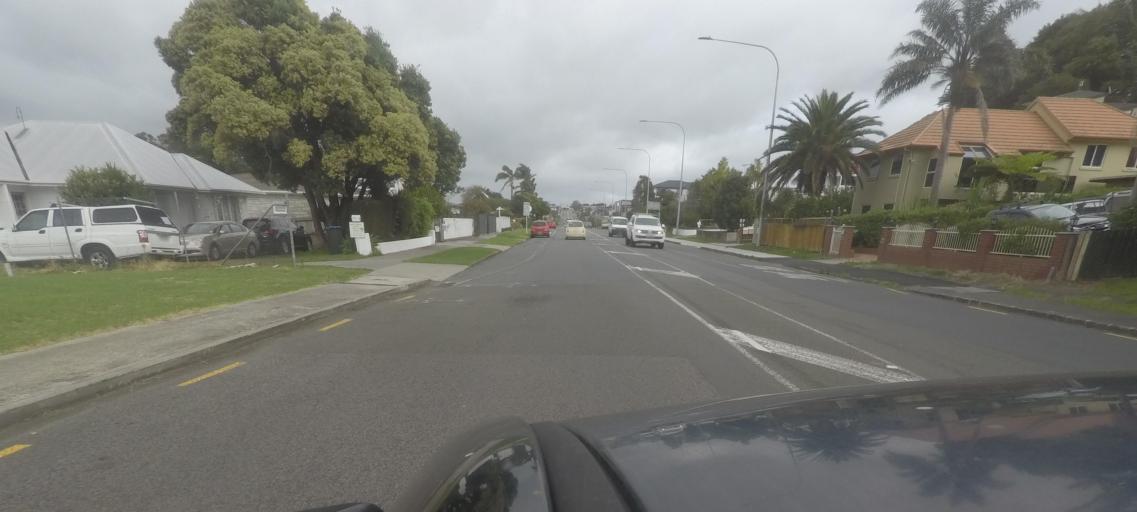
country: NZ
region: Auckland
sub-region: Auckland
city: Auckland
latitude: -36.9124
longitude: 174.7393
